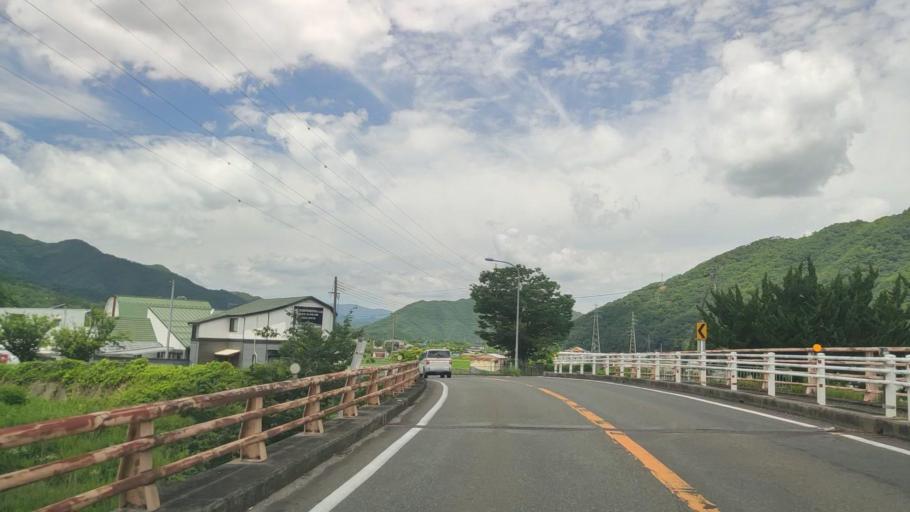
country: JP
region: Hyogo
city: Toyooka
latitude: 35.3547
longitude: 134.8378
